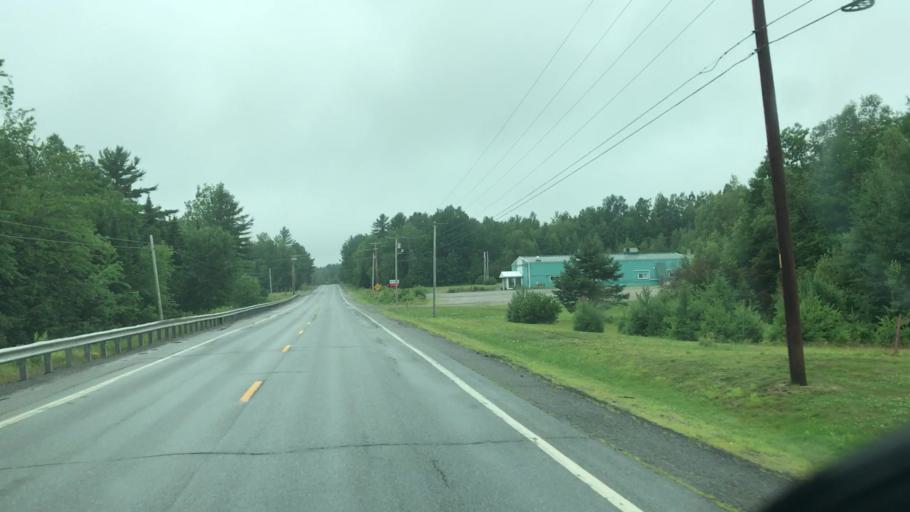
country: US
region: Maine
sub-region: Penobscot County
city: Enfield
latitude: 45.3301
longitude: -68.5872
